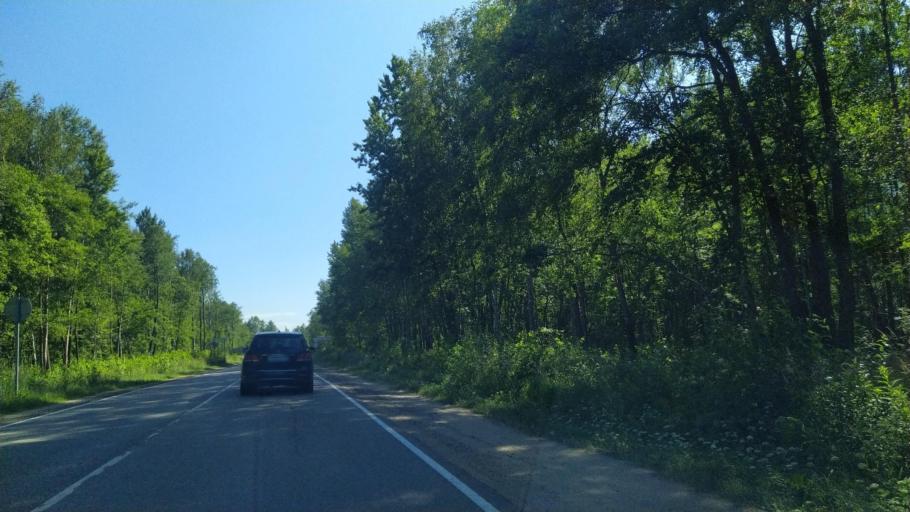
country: RU
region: Leningrad
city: Borisova Griva
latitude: 60.1109
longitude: 31.0838
